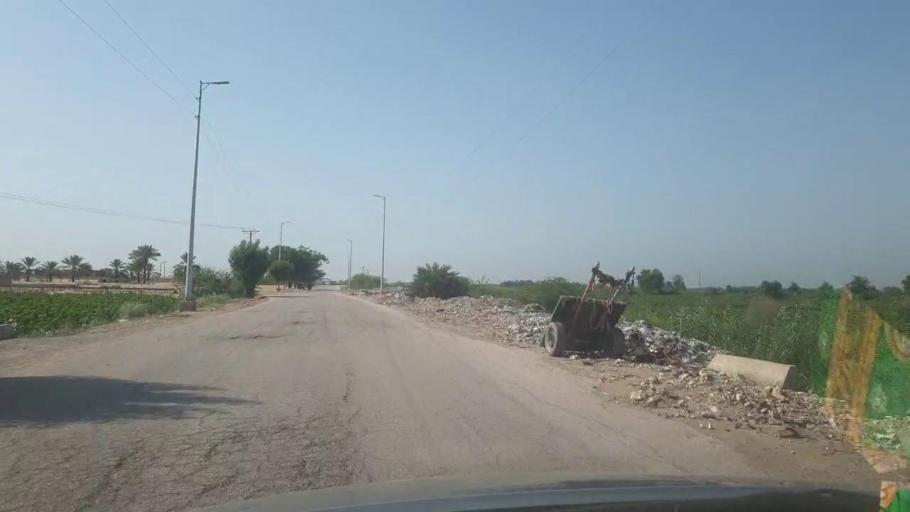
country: PK
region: Sindh
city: Rohri
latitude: 27.5075
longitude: 69.0367
